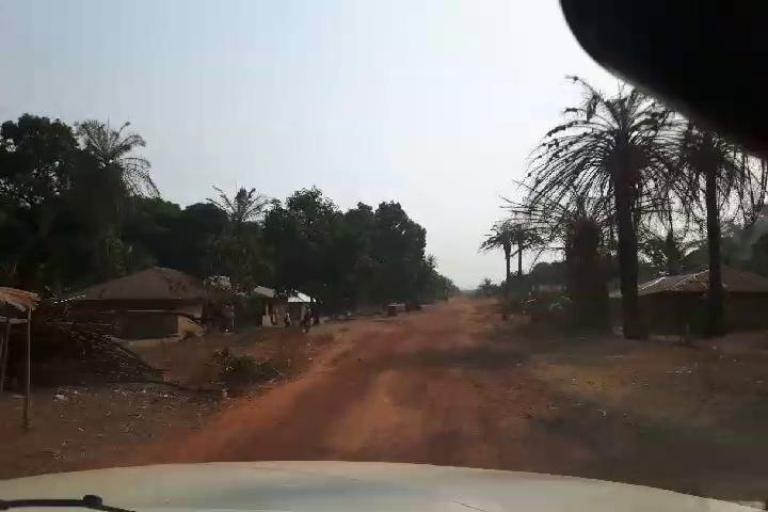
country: SL
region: Northern Province
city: Masingbi
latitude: 8.8260
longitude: -11.8543
